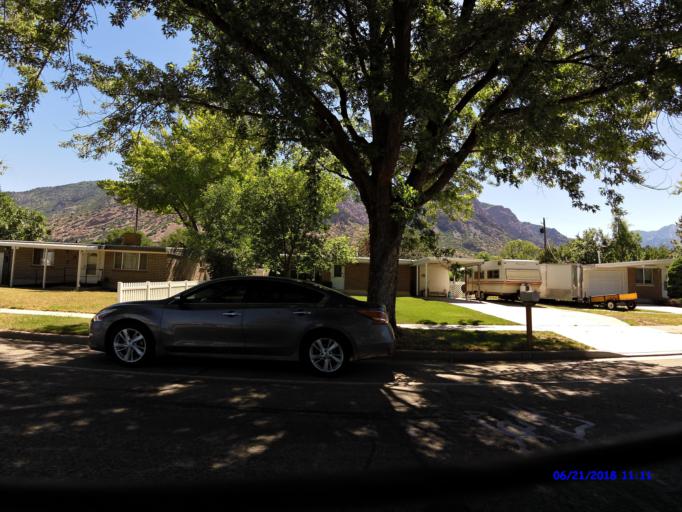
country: US
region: Utah
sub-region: Weber County
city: Harrisville
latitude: 41.2733
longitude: -111.9591
